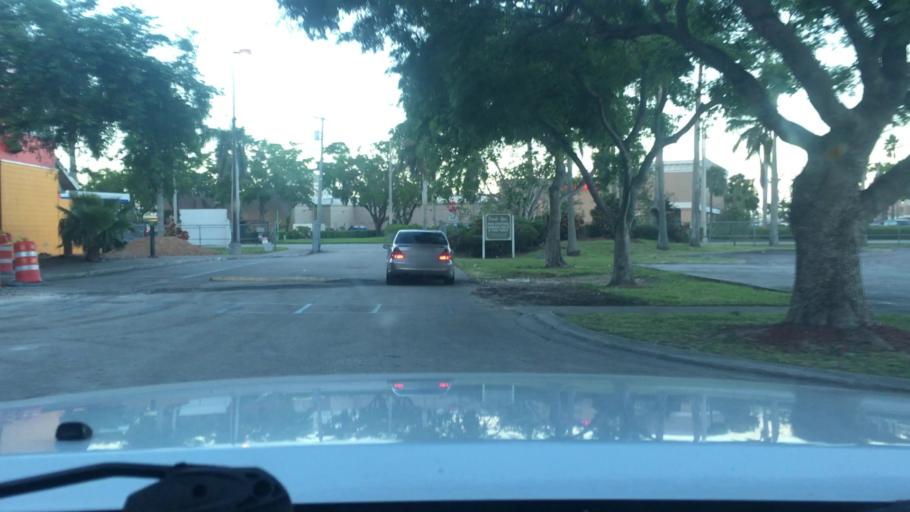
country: US
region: Florida
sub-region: Miami-Dade County
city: Homestead
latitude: 25.4766
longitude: -80.4640
